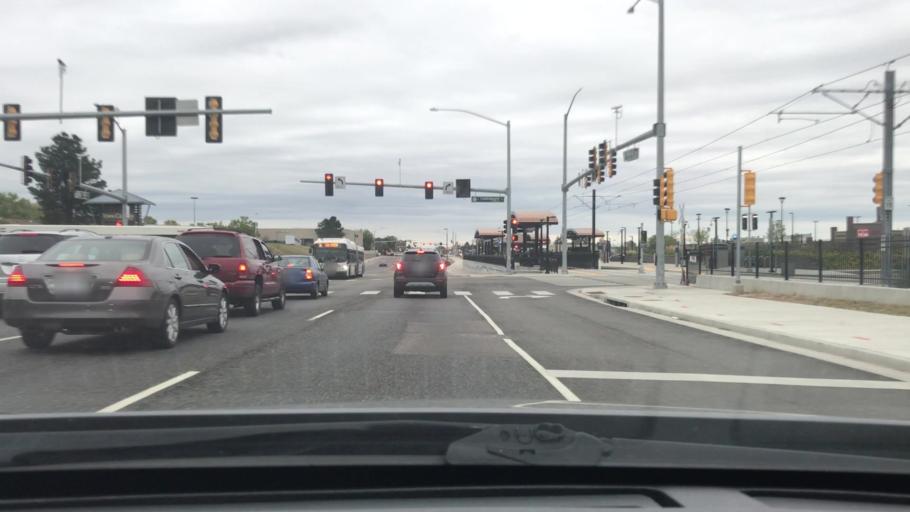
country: US
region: Colorado
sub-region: Adams County
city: Aurora
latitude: 39.7073
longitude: -104.8192
